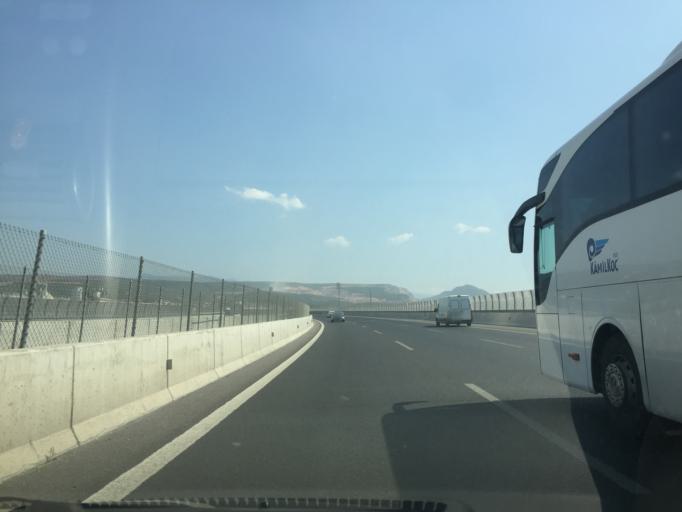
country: TR
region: Izmir
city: Bornova
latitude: 38.4435
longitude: 27.2552
